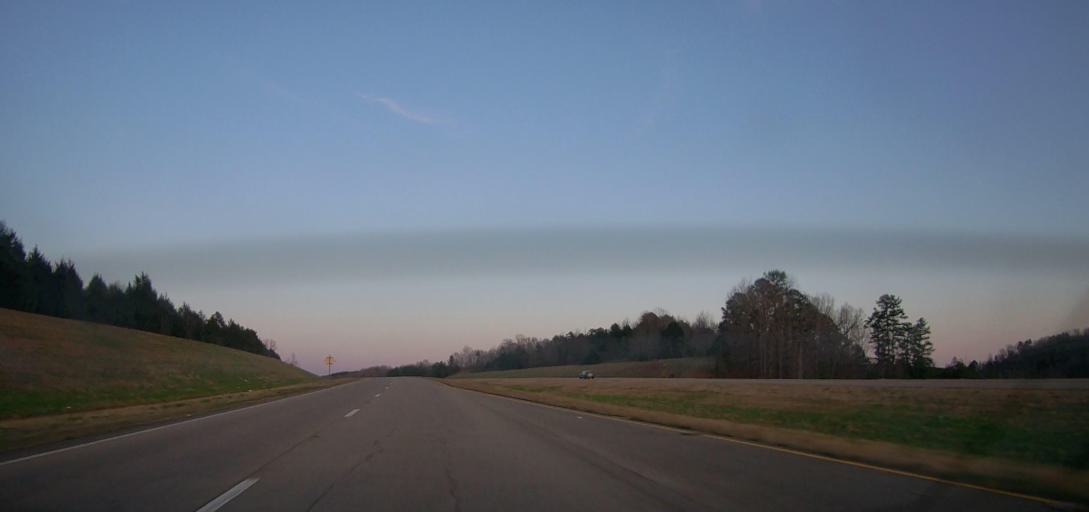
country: US
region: Mississippi
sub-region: Alcorn County
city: Corinth
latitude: 34.9327
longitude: -88.7660
